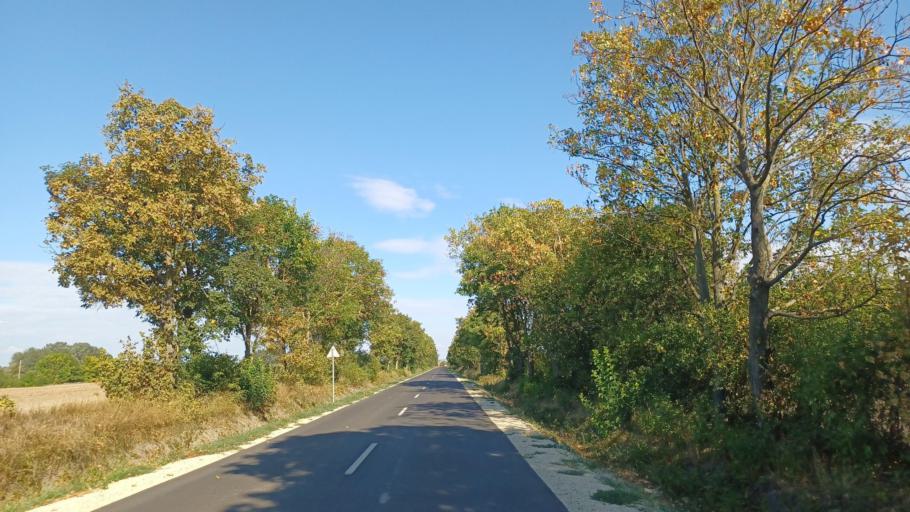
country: HU
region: Tolna
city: Dunaszentgyorgy
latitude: 46.4997
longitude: 18.8275
